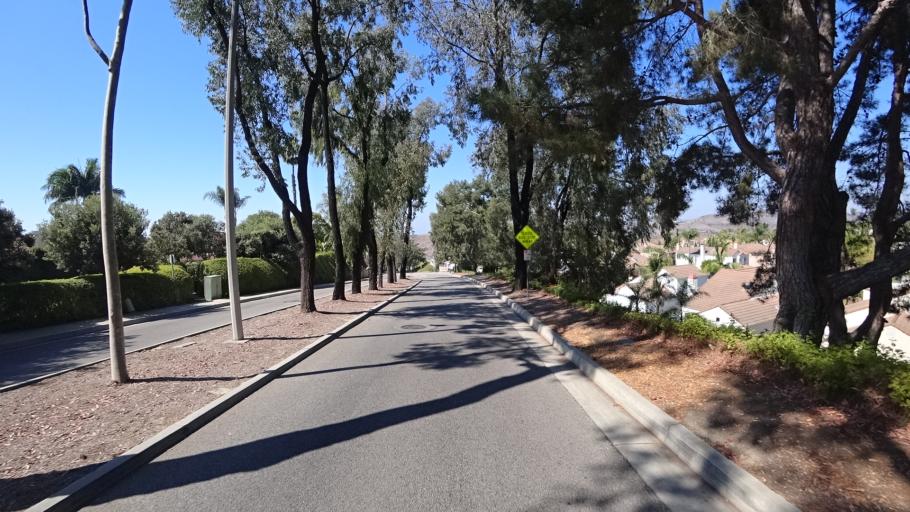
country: US
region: California
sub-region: Orange County
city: San Clemente
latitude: 33.4451
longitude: -117.6004
